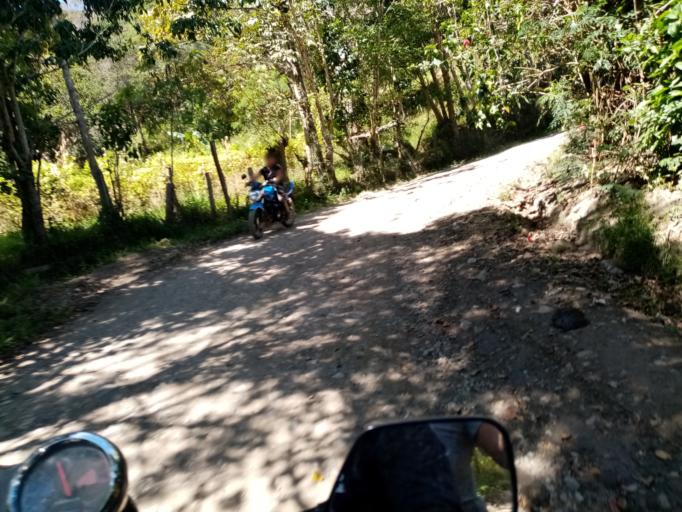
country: CO
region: Cundinamarca
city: Tenza
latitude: 5.0759
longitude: -73.4254
